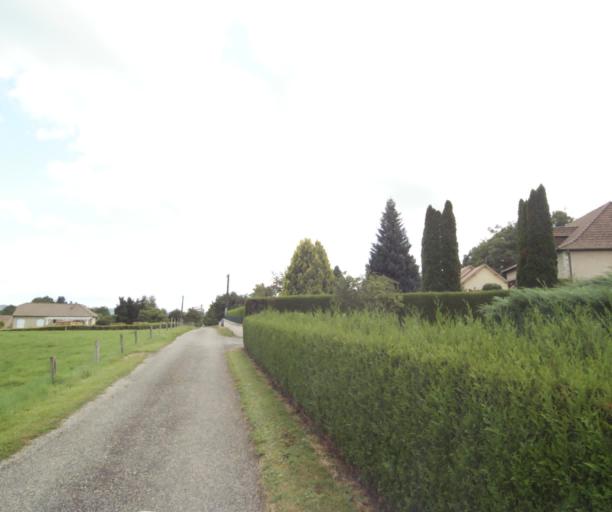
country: FR
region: Limousin
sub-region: Departement de la Correze
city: Sainte-Fortunade
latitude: 45.1990
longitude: 1.8183
